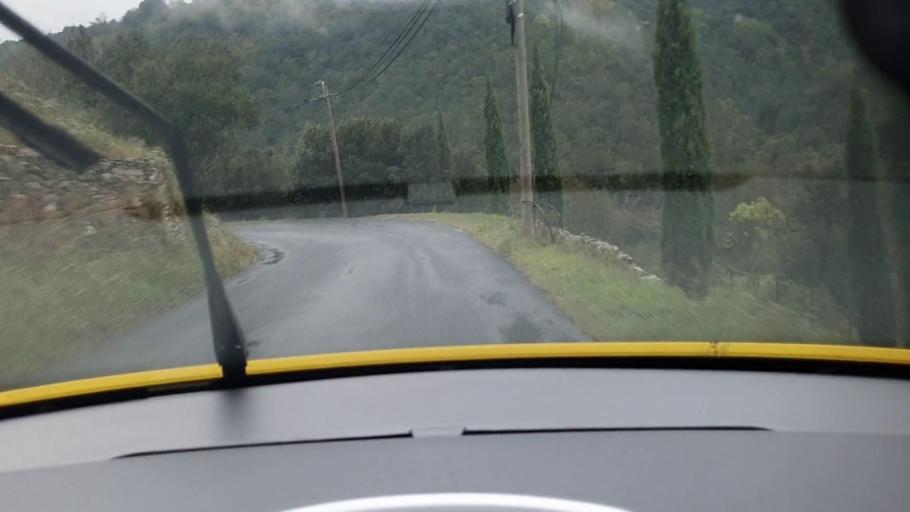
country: FR
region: Languedoc-Roussillon
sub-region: Departement du Gard
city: Sumene
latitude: 43.9945
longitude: 3.7126
